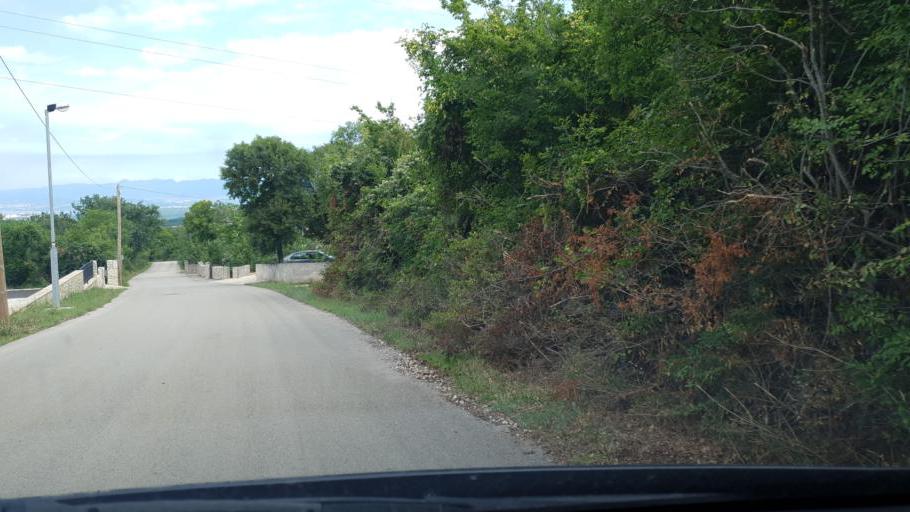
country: HR
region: Primorsko-Goranska
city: Njivice
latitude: 45.1289
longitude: 14.5843
